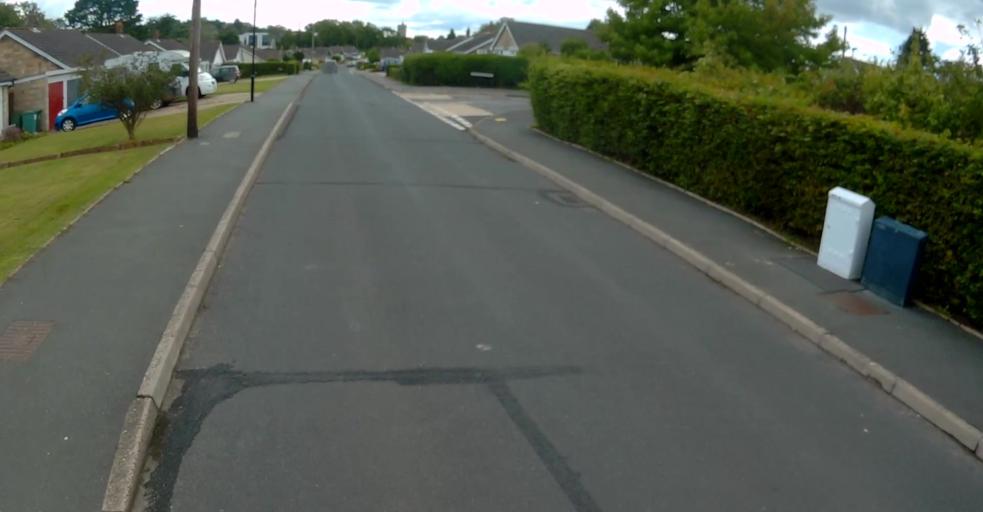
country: GB
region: England
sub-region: Isle of Wight
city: Newport
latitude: 50.6968
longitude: -1.3084
